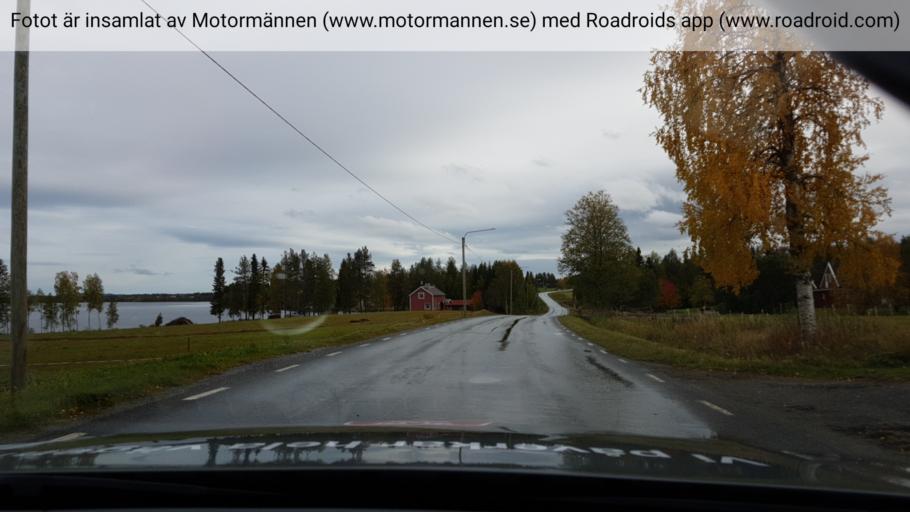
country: SE
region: Vaesterbotten
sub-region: Vilhelmina Kommun
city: Sjoberg
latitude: 64.6461
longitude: 16.3490
